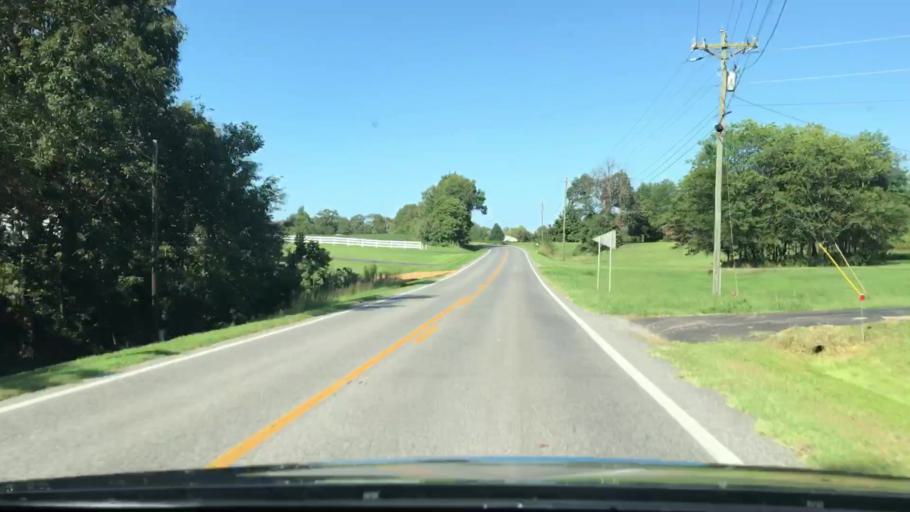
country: US
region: Kentucky
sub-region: Graves County
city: Mayfield
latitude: 36.7657
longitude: -88.5725
